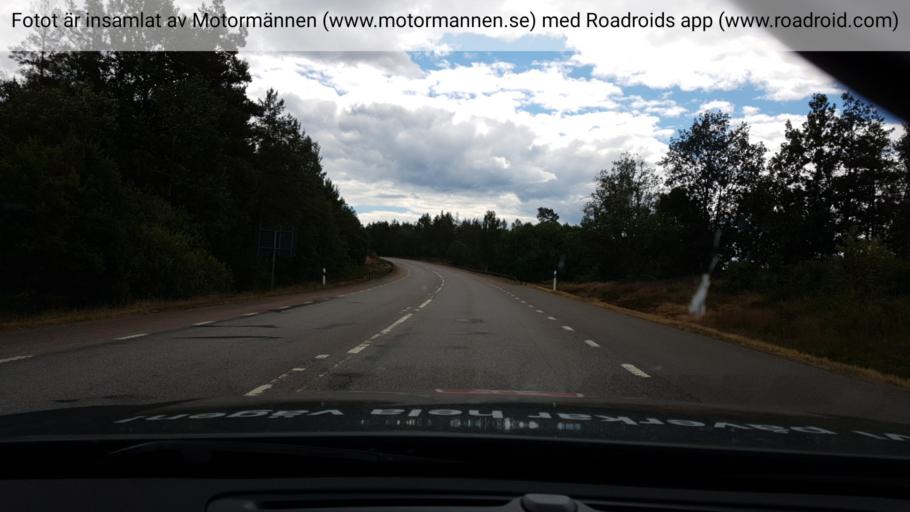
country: SE
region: Kalmar
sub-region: Vasterviks Kommun
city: Ankarsrum
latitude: 57.6423
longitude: 16.4442
